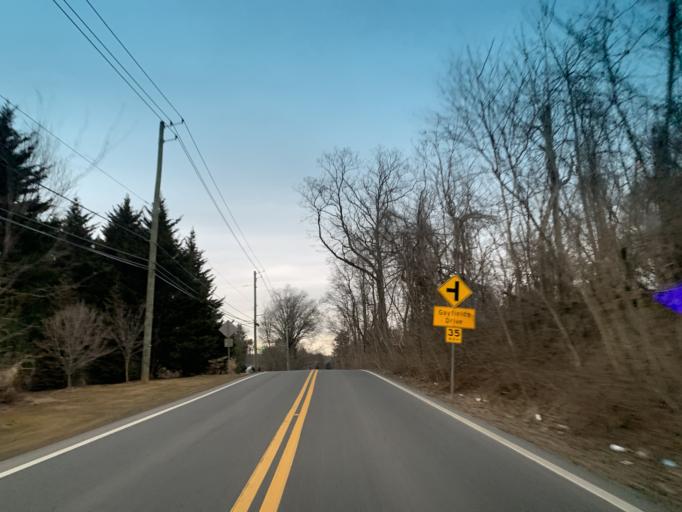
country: US
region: Maryland
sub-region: Montgomery County
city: Layhill
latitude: 39.1086
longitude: -77.0370
